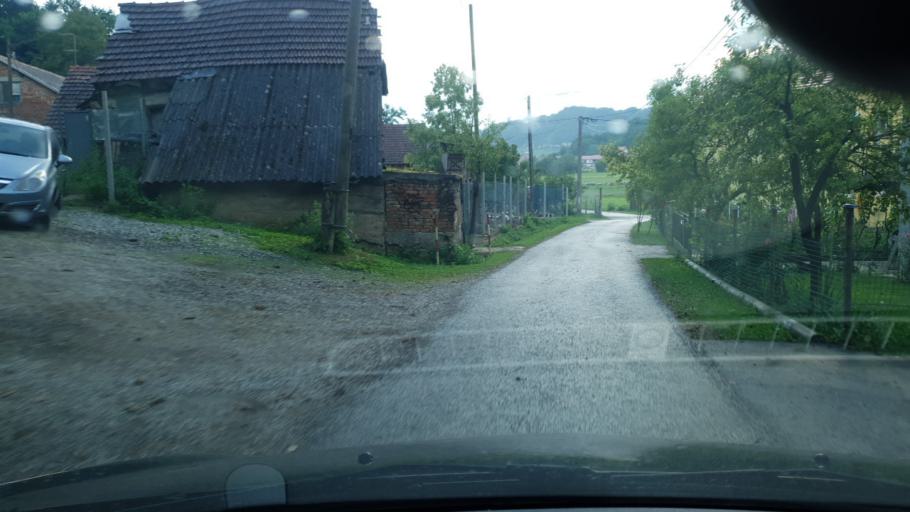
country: HR
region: Krapinsko-Zagorska
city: Radoboj
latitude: 46.1001
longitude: 15.9137
